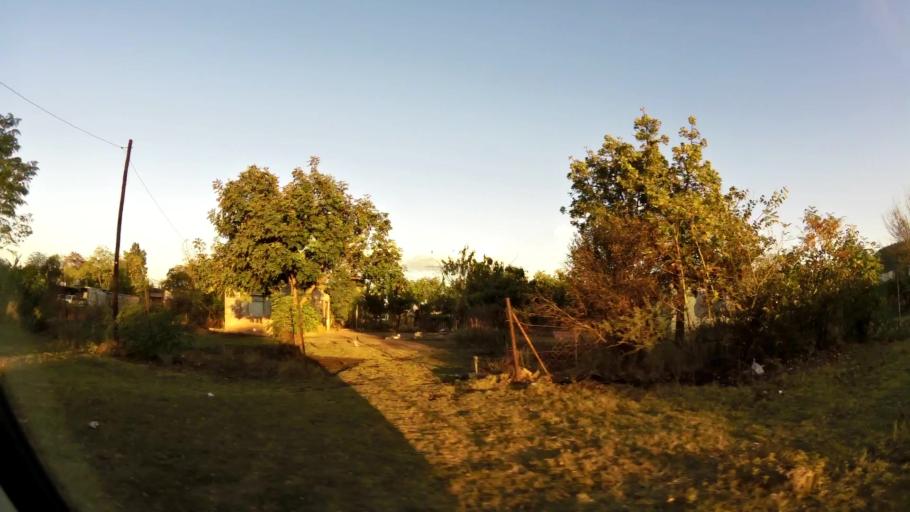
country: ZA
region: Limpopo
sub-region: Waterberg District Municipality
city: Mokopane
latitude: -24.1468
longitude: 28.9745
